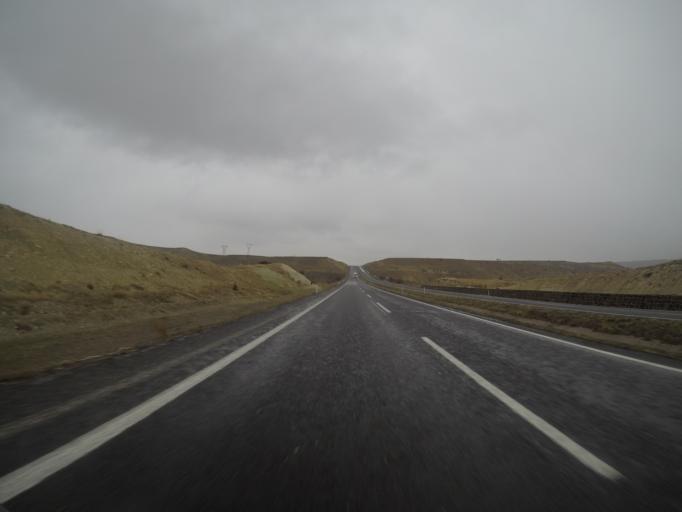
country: TR
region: Nevsehir
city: Urgub
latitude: 38.7422
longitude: 35.0074
